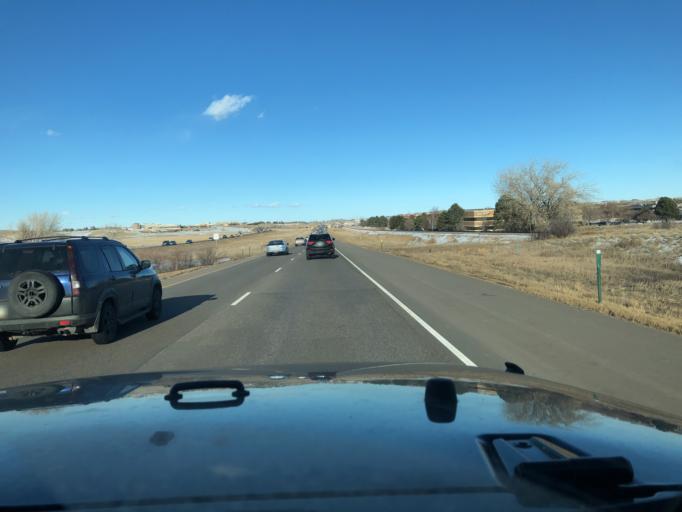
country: US
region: Colorado
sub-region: Boulder County
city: Gunbarrel
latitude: 40.0671
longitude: -105.2143
